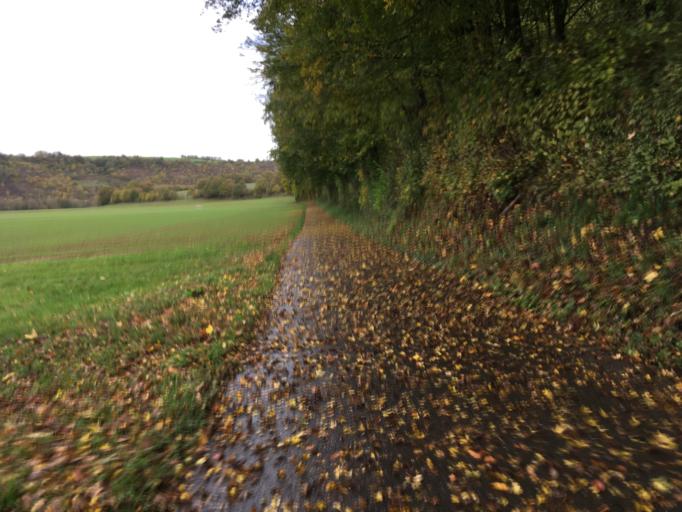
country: DE
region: Baden-Wuerttemberg
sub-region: Regierungsbezirk Stuttgart
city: Widdern
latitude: 49.3126
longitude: 9.3976
